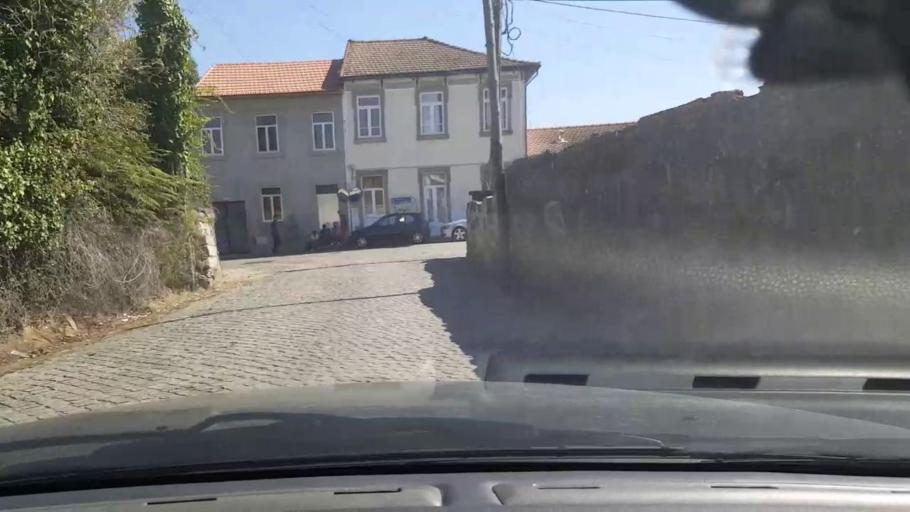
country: PT
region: Porto
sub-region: Matosinhos
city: Lavra
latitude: 41.2667
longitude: -8.6966
